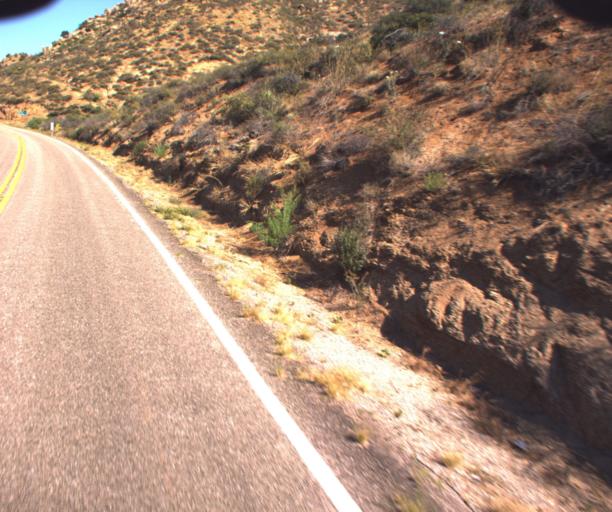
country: US
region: Arizona
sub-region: Graham County
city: Swift Trail Junction
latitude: 32.5761
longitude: -109.8415
